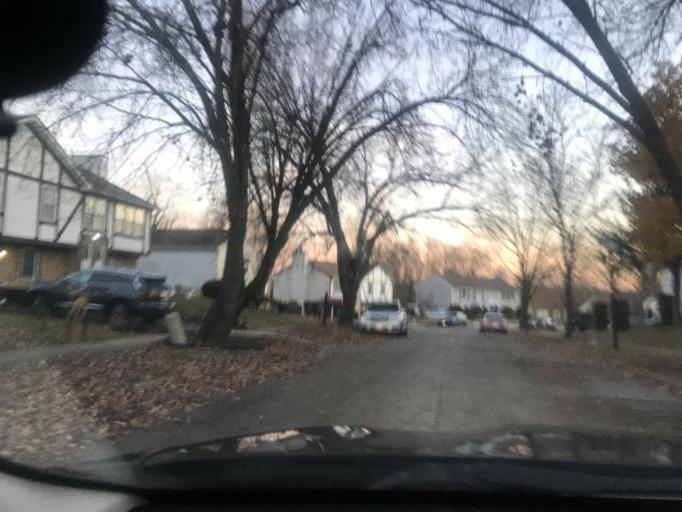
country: US
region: Maryland
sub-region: Prince George's County
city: Oxon Hill
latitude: 38.7989
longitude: -76.9756
